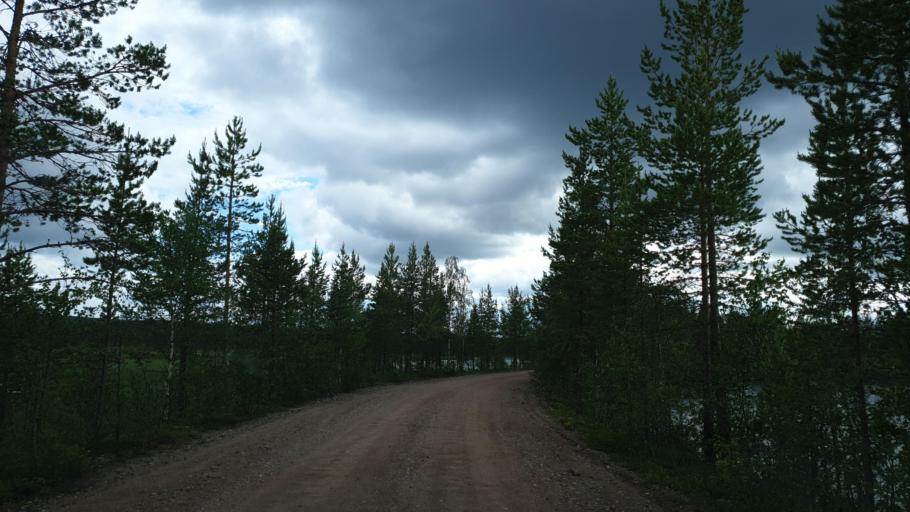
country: SE
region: Jaemtland
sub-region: Harjedalens Kommun
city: Sveg
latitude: 62.0350
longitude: 14.4936
